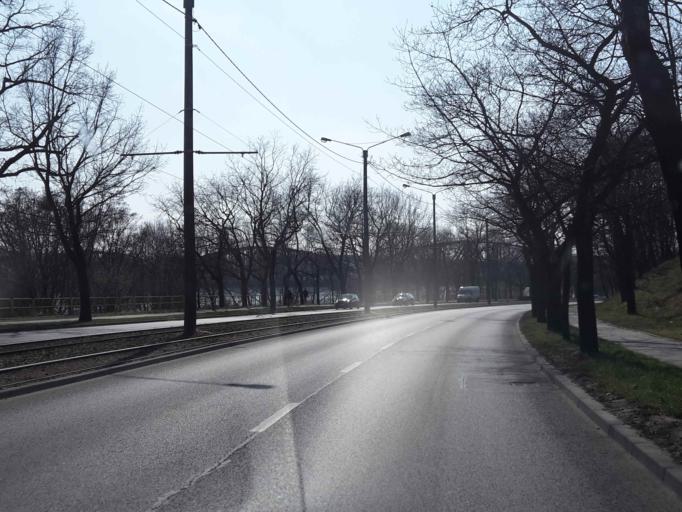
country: PL
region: Kujawsko-Pomorskie
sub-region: Torun
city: Torun
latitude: 53.0124
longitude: 18.6250
